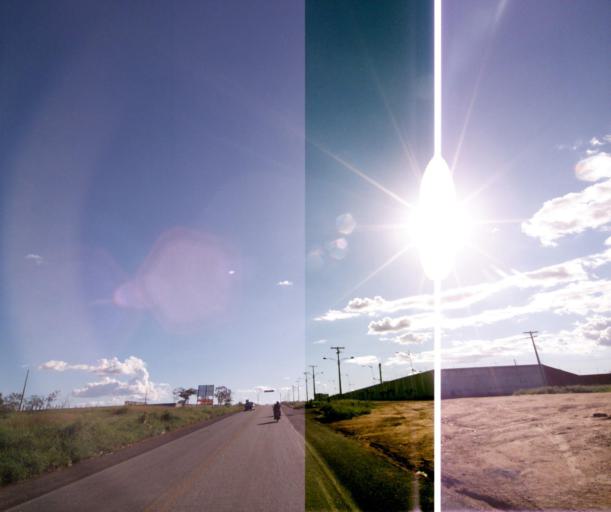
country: BR
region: Bahia
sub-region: Guanambi
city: Guanambi
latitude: -14.1974
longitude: -42.7513
